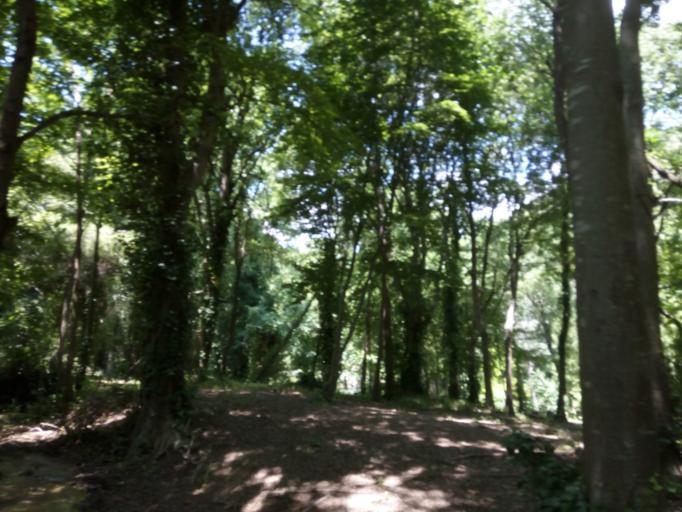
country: HR
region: Sibensko-Kniniska
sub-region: Grad Sibenik
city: Sibenik
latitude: 43.8068
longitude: 15.9640
